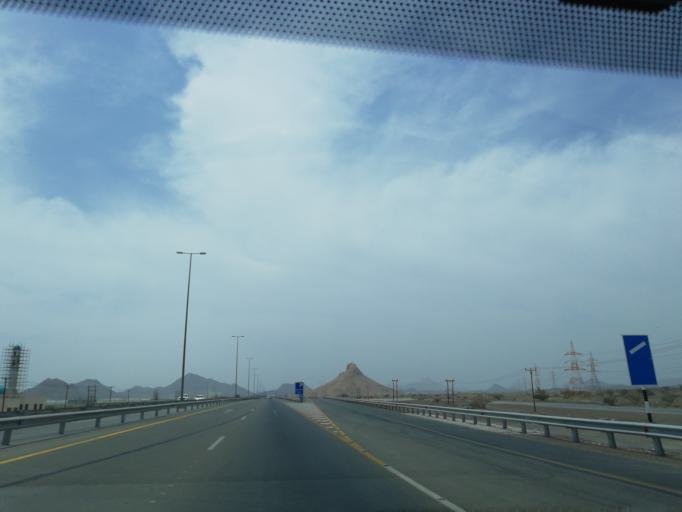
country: OM
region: Muhafazat ad Dakhiliyah
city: Nizwa
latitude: 22.8581
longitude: 57.5047
